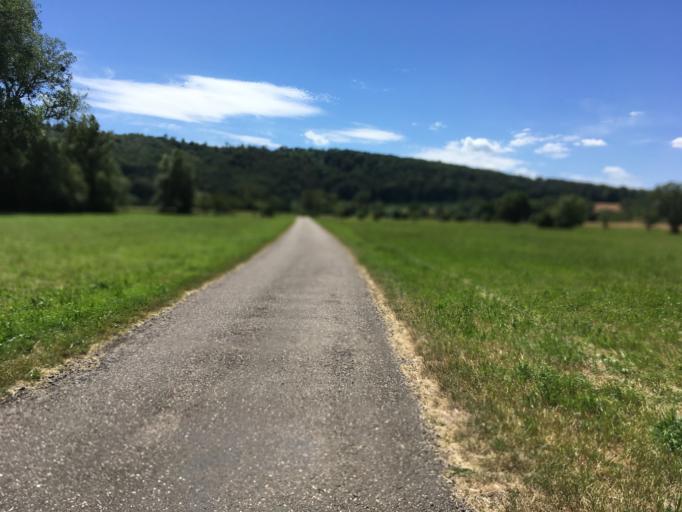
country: DE
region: Baden-Wuerttemberg
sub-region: Karlsruhe Region
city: Illingen
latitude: 48.9313
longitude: 8.9147
